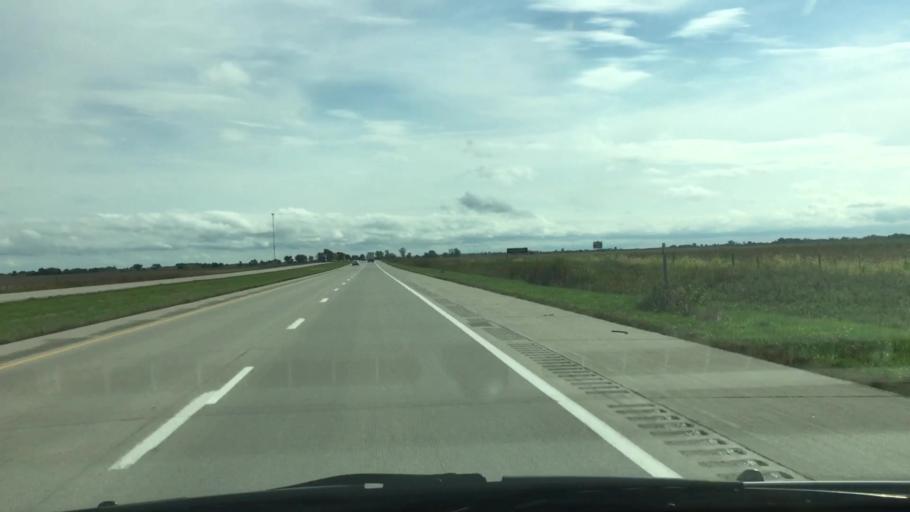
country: US
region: Iowa
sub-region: Clarke County
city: Osceola
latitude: 40.9373
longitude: -93.7990
